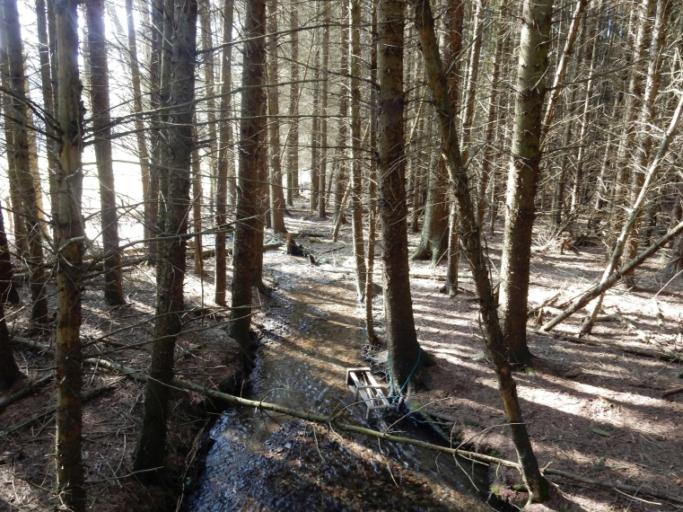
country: LU
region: Diekirch
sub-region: Canton de Wiltz
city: Winseler
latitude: 49.9921
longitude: 5.8581
